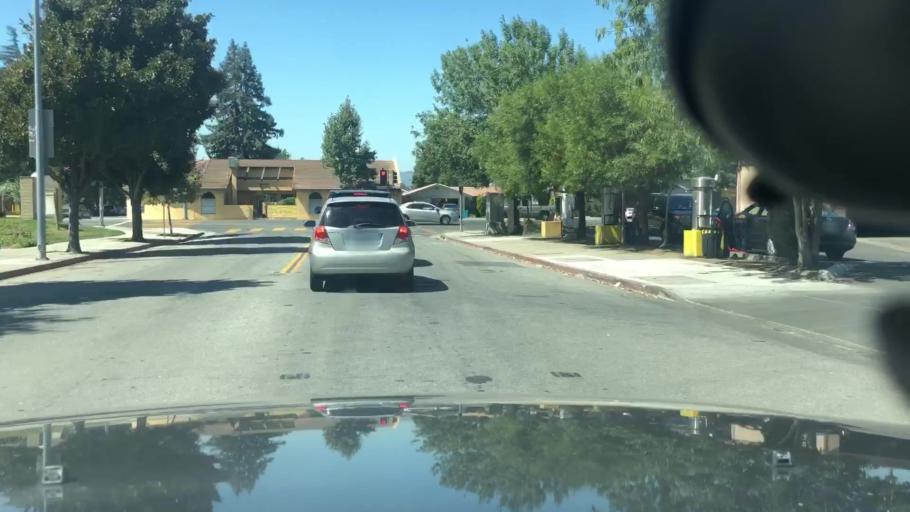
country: US
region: California
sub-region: Santa Clara County
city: Campbell
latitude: 37.2819
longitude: -121.9491
